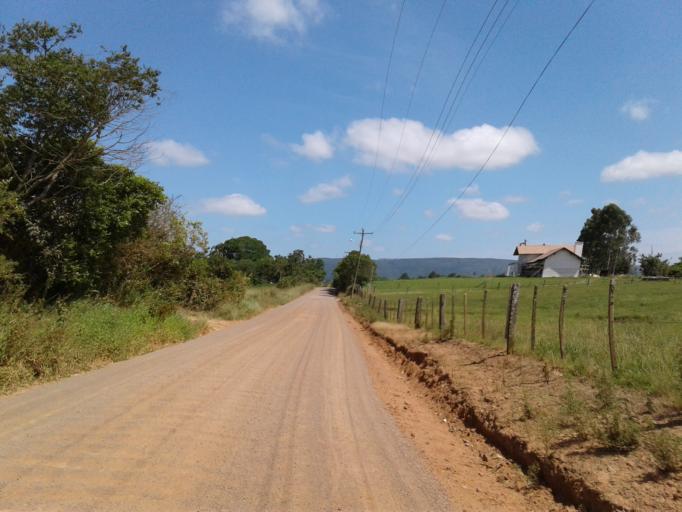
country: BR
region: Rio Grande do Sul
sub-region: Gravatai
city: Gravatai
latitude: -29.8790
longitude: -50.8175
